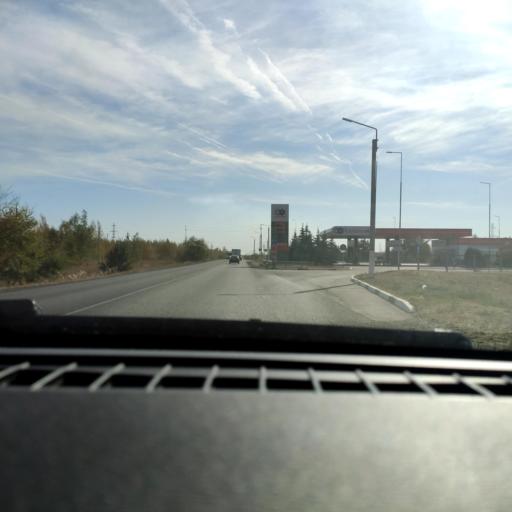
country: RU
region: Voronezj
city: Maslovka
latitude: 51.5872
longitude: 39.2541
